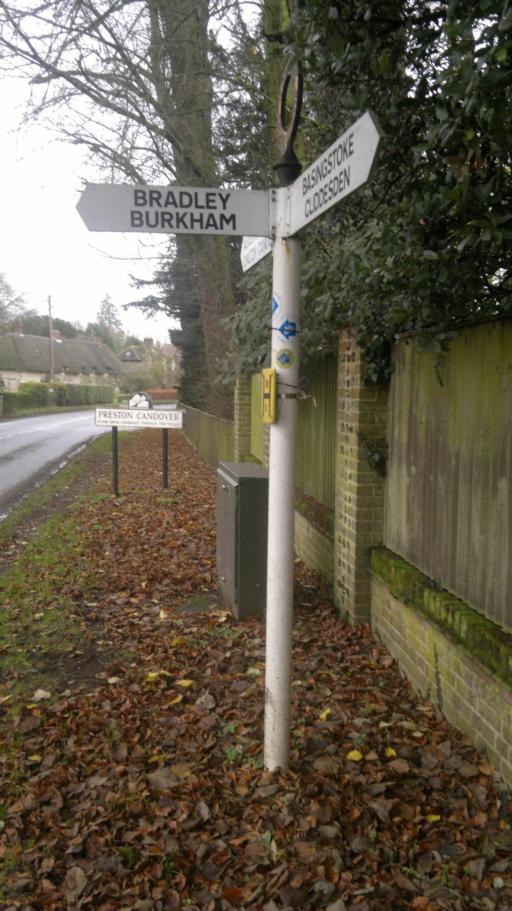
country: GB
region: England
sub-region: Hampshire
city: Basingstoke
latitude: 51.1756
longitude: -1.1301
